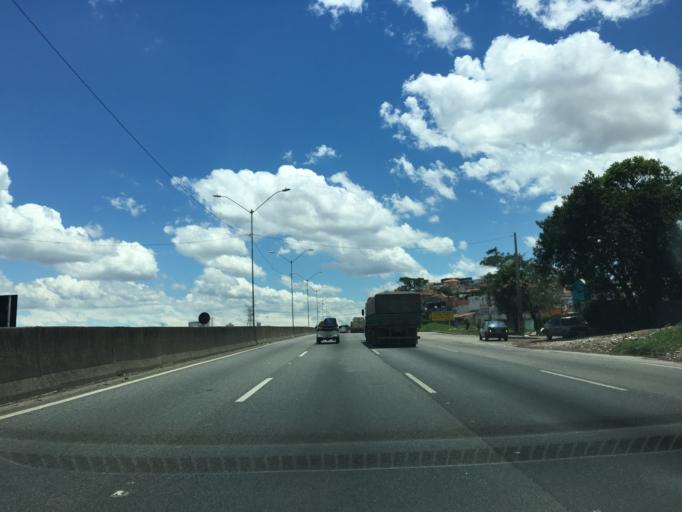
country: BR
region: Sao Paulo
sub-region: Guarulhos
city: Guarulhos
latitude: -23.4511
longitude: -46.5702
